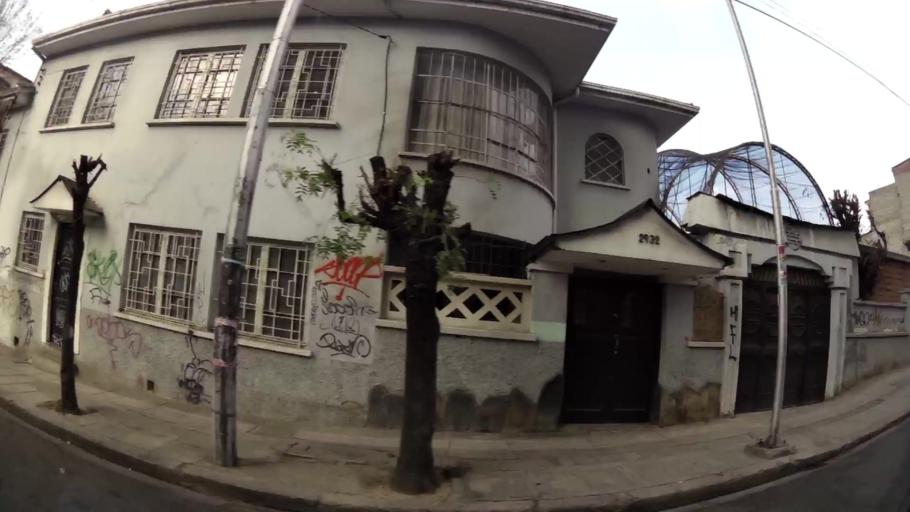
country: BO
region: La Paz
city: La Paz
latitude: -16.5149
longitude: -68.1207
